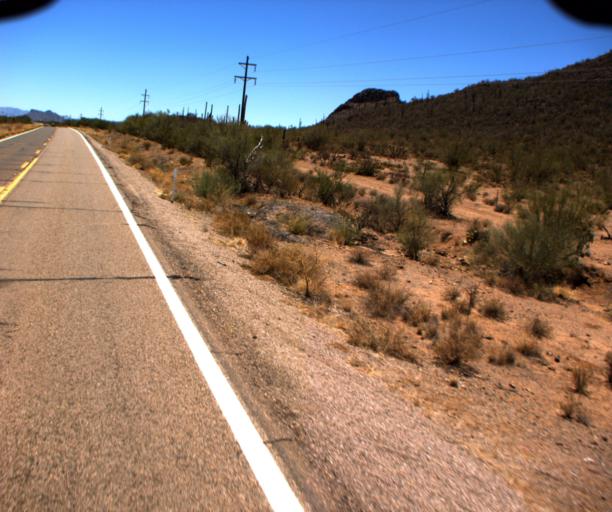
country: US
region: Arizona
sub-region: Pima County
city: Sells
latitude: 31.9565
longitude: -111.9456
